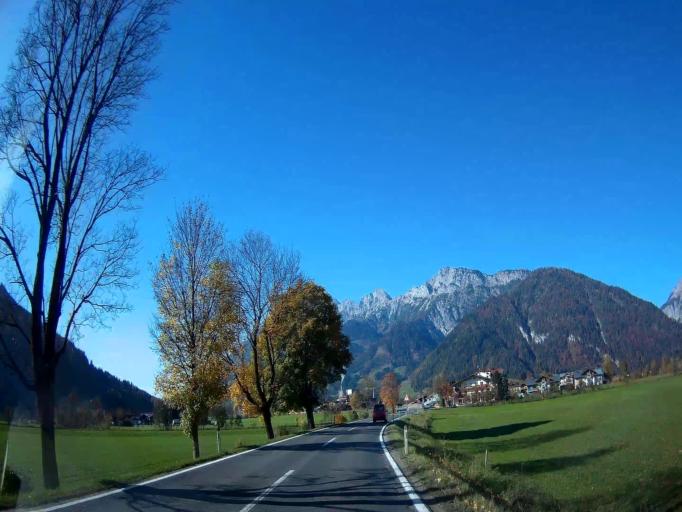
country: AT
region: Salzburg
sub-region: Politischer Bezirk Zell am See
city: Saalfelden am Steinernen Meer
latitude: 47.4372
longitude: 12.8221
